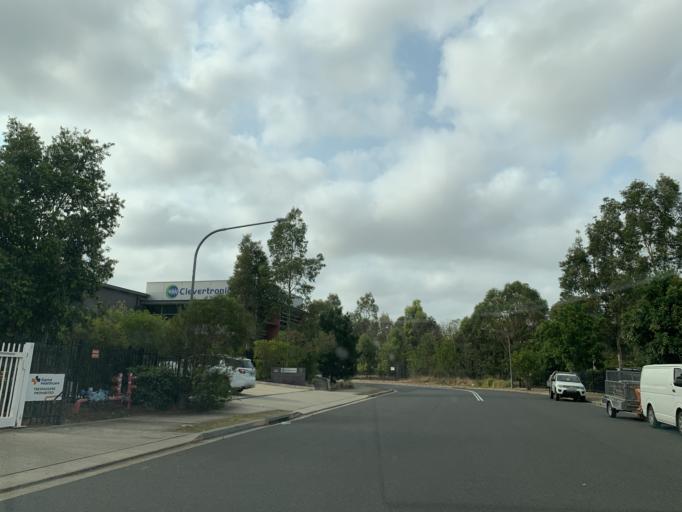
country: AU
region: New South Wales
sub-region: Holroyd
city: Girraween
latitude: -33.7758
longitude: 150.9475
